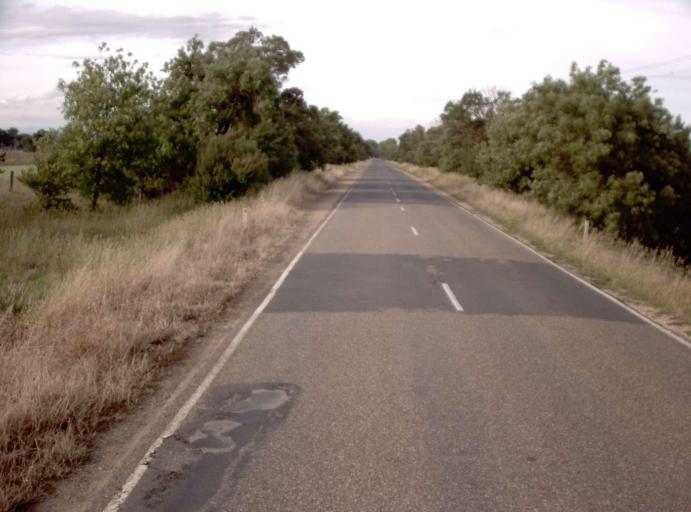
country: AU
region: Victoria
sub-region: Wellington
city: Heyfield
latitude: -37.9737
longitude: 146.8896
